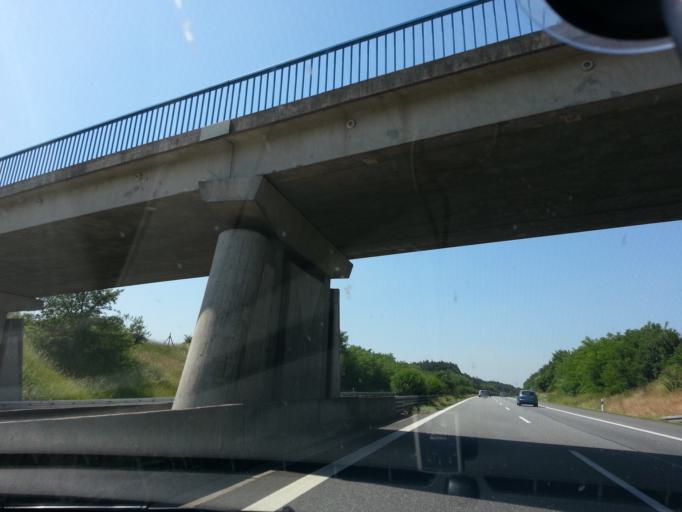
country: DE
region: Mecklenburg-Vorpommern
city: Locknitz
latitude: 53.3537
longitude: 11.7737
